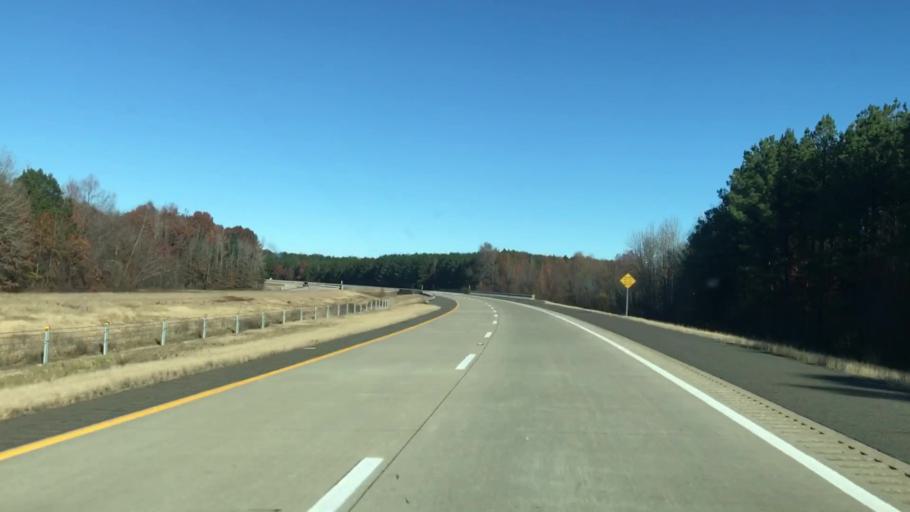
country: US
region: Texas
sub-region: Bowie County
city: Texarkana
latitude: 33.2385
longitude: -93.8730
